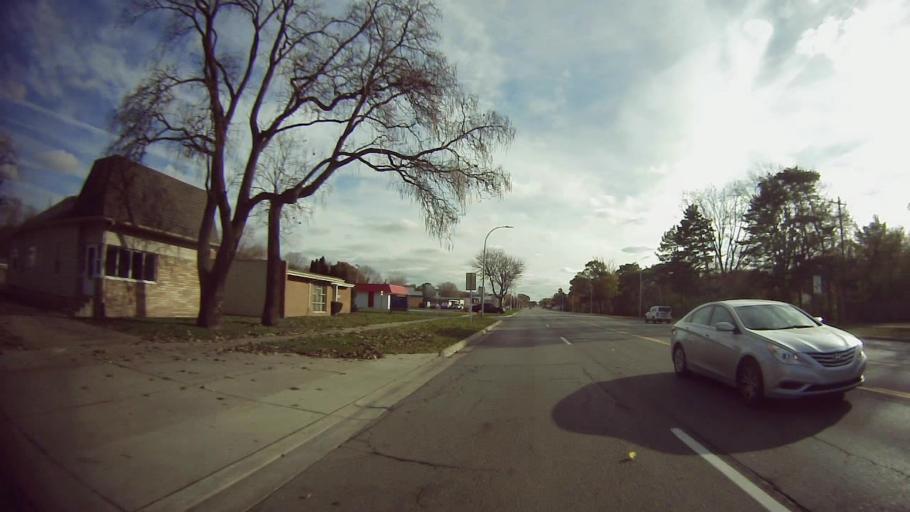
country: US
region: Michigan
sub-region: Oakland County
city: Oak Park
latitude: 42.4602
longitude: -83.1623
